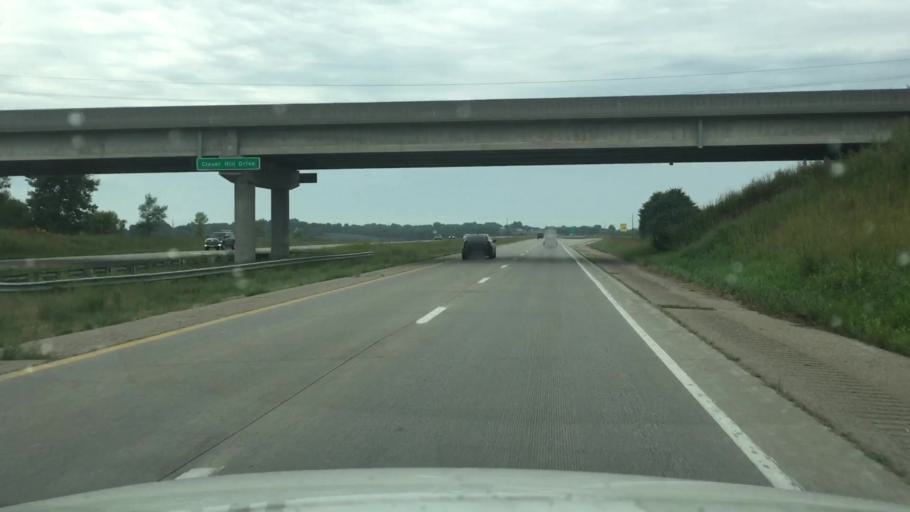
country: US
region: Iowa
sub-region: Warren County
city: Norwalk
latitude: 41.4983
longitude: -93.6157
